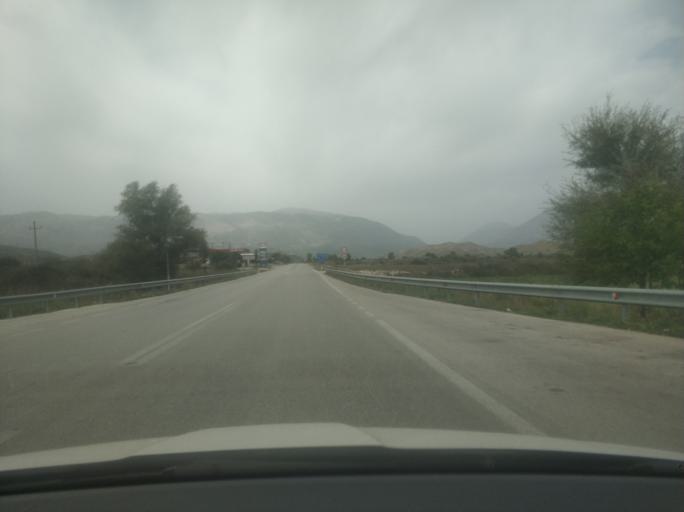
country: AL
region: Gjirokaster
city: Gjirokaster
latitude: 40.1216
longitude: 20.1141
